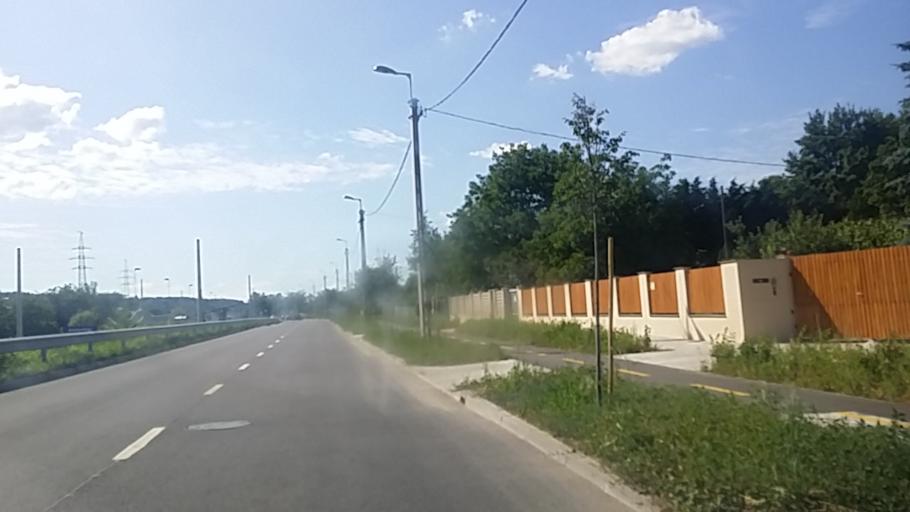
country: HU
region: Pest
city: Urom
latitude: 47.5727
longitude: 19.0205
